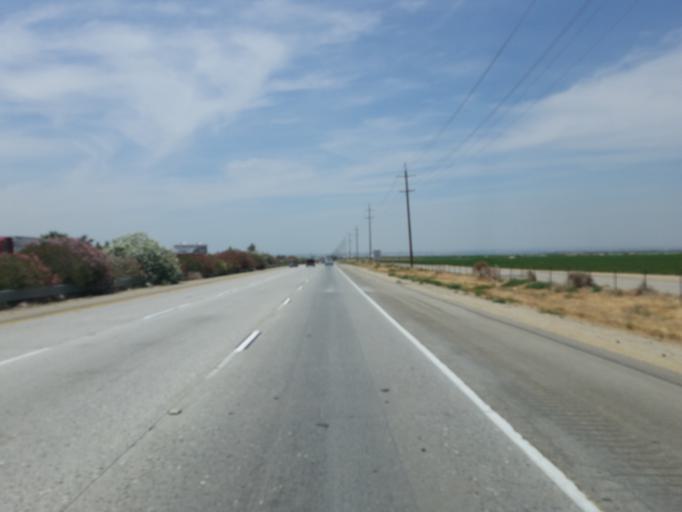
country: US
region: California
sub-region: Kern County
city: Weedpatch
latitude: 35.0636
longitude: -118.9696
